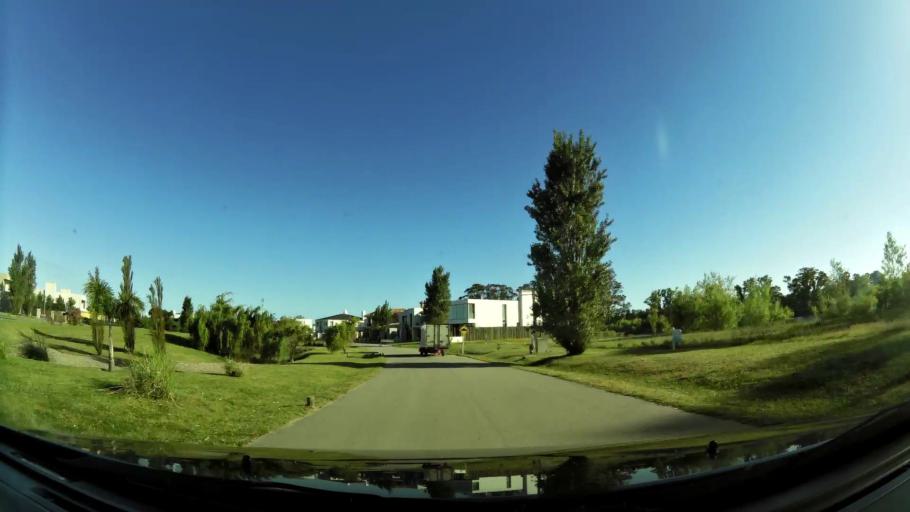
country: UY
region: Canelones
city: Paso de Carrasco
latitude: -34.8651
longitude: -56.0444
